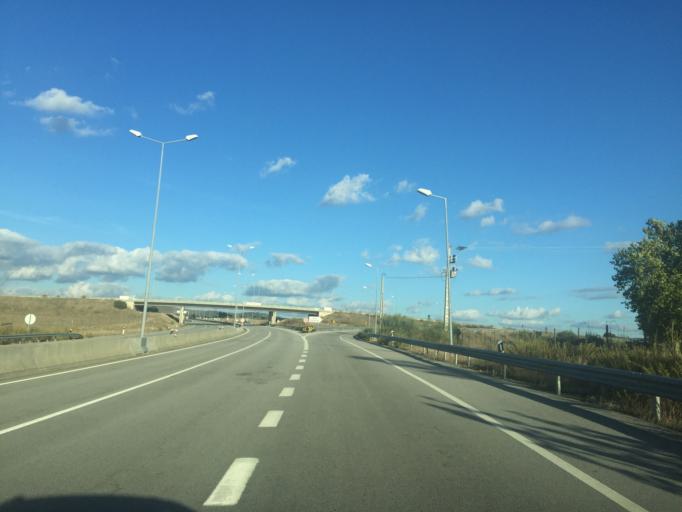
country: PT
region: Portalegre
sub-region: Alter do Chao
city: Alter do Chao
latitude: 39.1970
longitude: -7.6991
